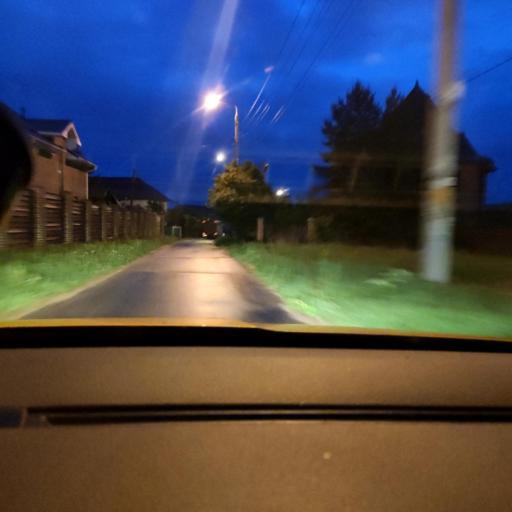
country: RU
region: Moskovskaya
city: Dmitrov
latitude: 56.3471
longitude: 37.5400
